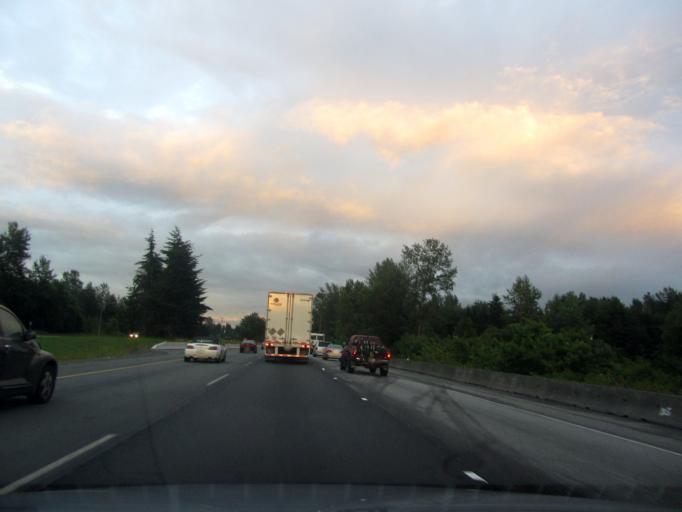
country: CA
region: British Columbia
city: Aldergrove
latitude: 49.1051
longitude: -122.5025
